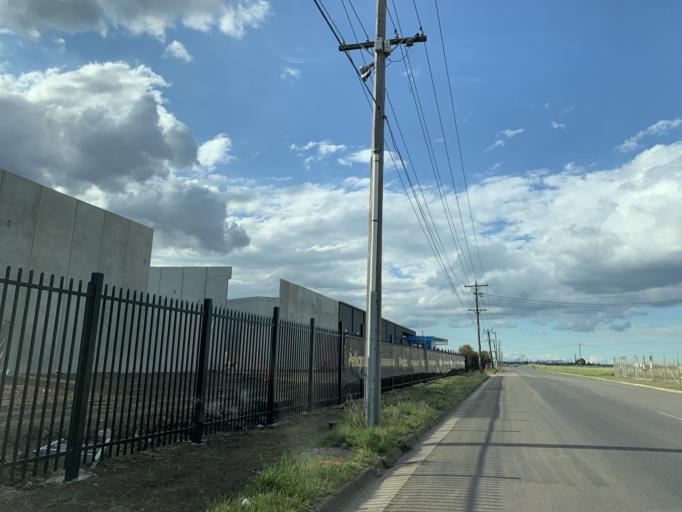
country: AU
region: Victoria
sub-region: Brimbank
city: Albion
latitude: -37.7630
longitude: 144.8405
